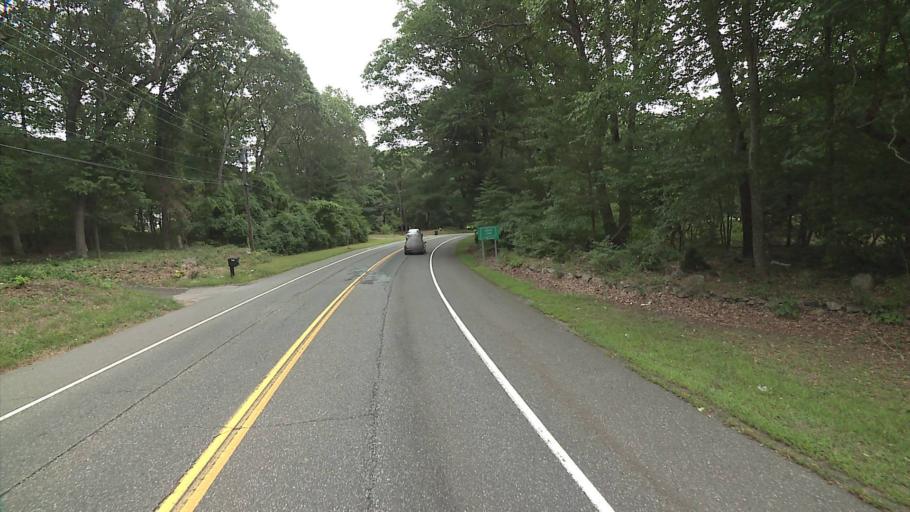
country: US
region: Connecticut
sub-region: New London County
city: Niantic
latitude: 41.2955
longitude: -72.2643
